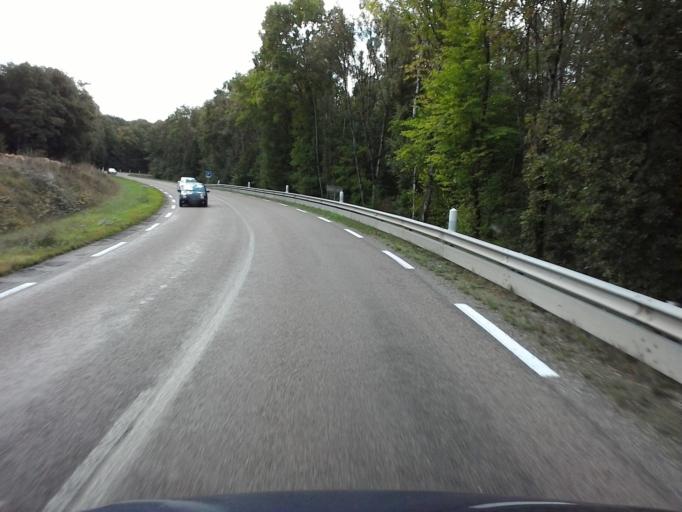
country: FR
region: Lorraine
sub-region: Departement des Vosges
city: Neufchateau
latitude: 48.3455
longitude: 5.6578
